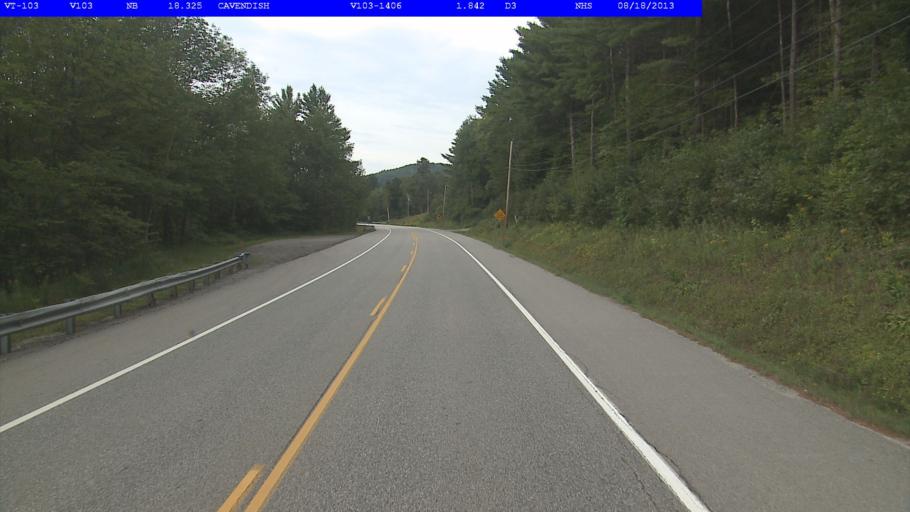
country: US
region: Vermont
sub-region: Windsor County
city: Chester
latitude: 43.3729
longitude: -72.6346
